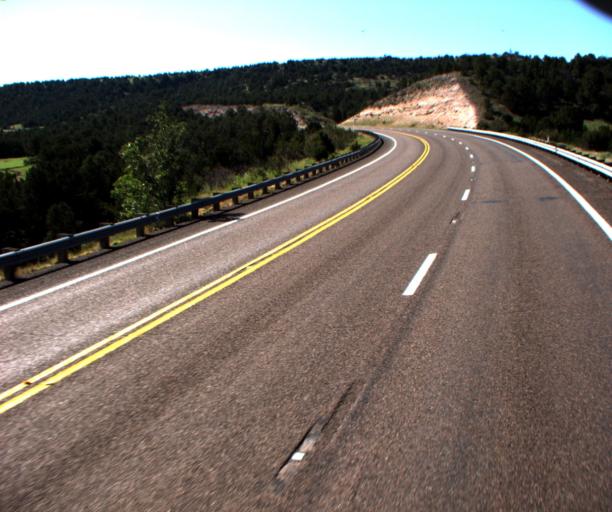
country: US
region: Arizona
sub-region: Apache County
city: Eagar
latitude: 34.0910
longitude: -109.2427
